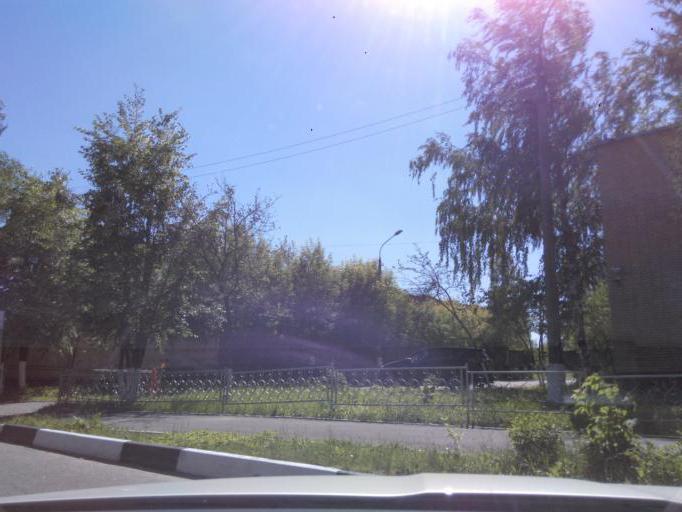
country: RU
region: Moskovskaya
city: Solnechnogorsk
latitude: 56.1853
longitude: 36.9668
